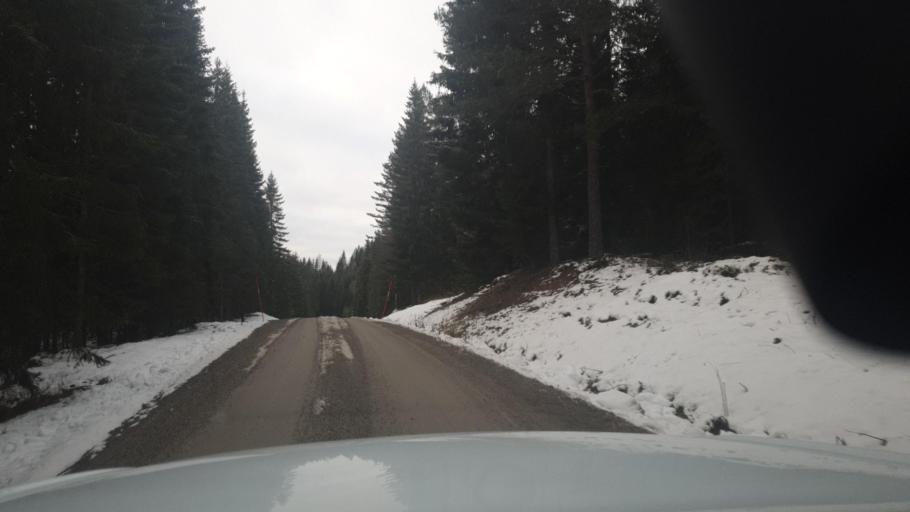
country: SE
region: Vaermland
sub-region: Sunne Kommun
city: Sunne
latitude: 59.8619
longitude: 12.8719
